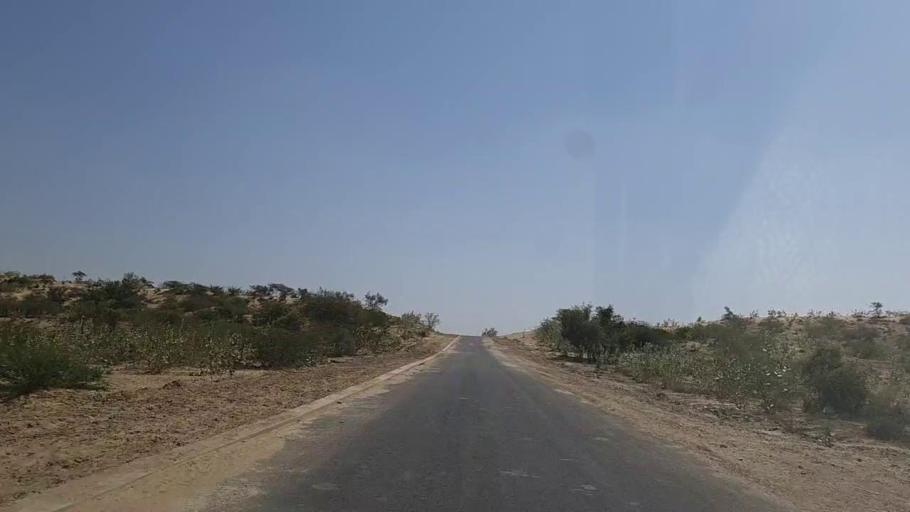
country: PK
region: Sindh
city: Diplo
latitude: 24.4851
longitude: 69.4675
